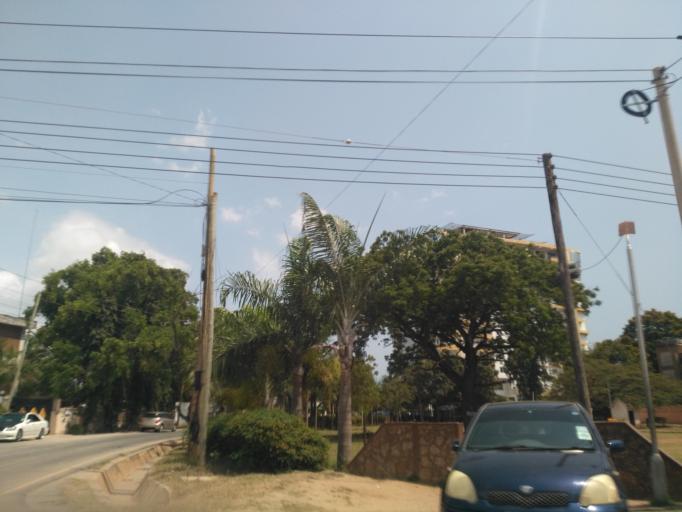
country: TZ
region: Dar es Salaam
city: Dar es Salaam
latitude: -6.7977
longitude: 39.2780
